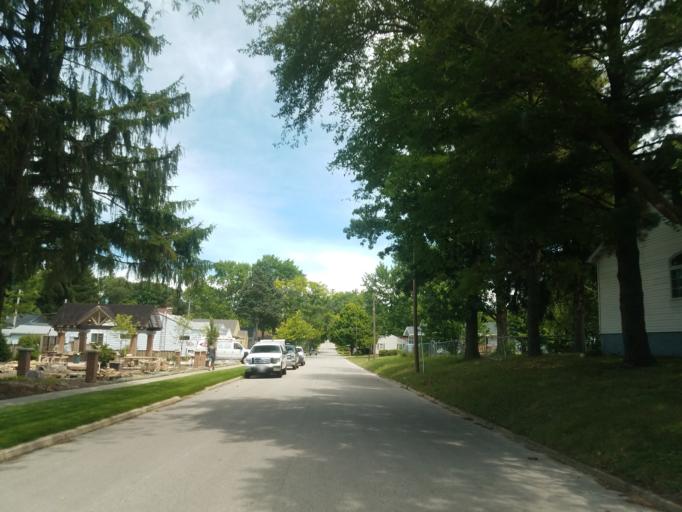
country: US
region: Illinois
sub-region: McLean County
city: Bloomington
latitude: 40.4678
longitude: -88.9837
